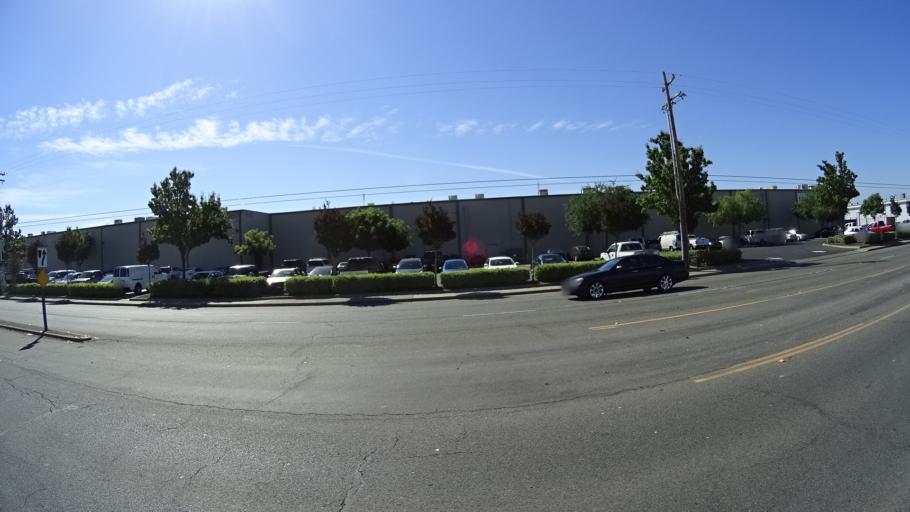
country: US
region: California
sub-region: Sacramento County
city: North Highlands
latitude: 38.6472
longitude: -121.3955
